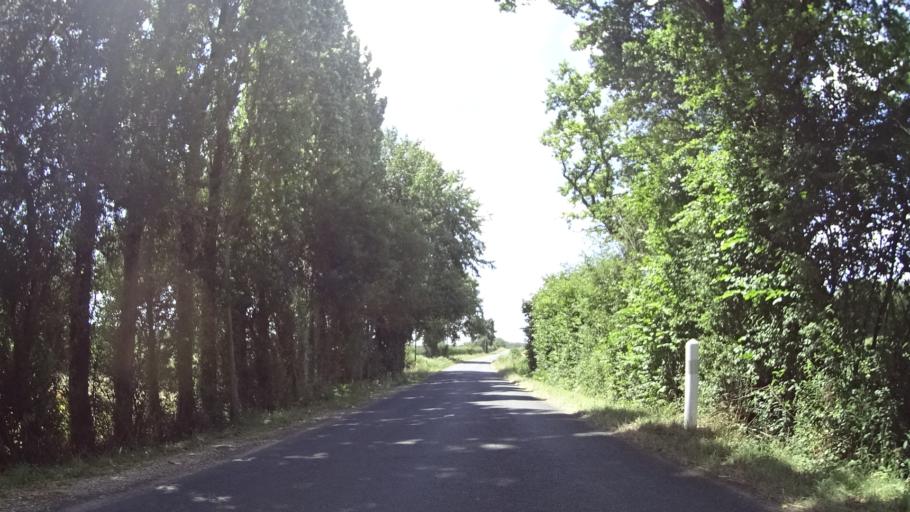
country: FR
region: Pays de la Loire
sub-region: Departement de Maine-et-Loire
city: Noyant-la-Gravoyere
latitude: 47.6158
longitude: -0.9613
